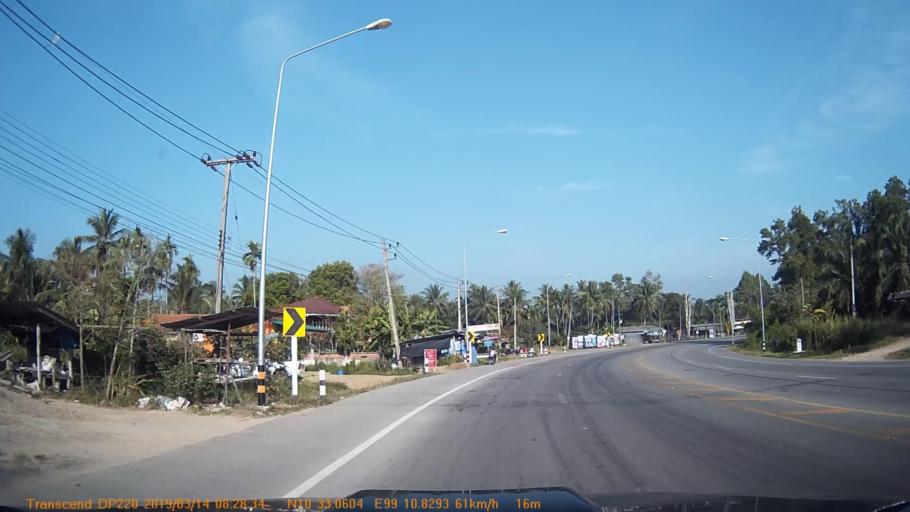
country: TH
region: Chumphon
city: Chumphon
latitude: 10.5511
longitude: 99.1804
